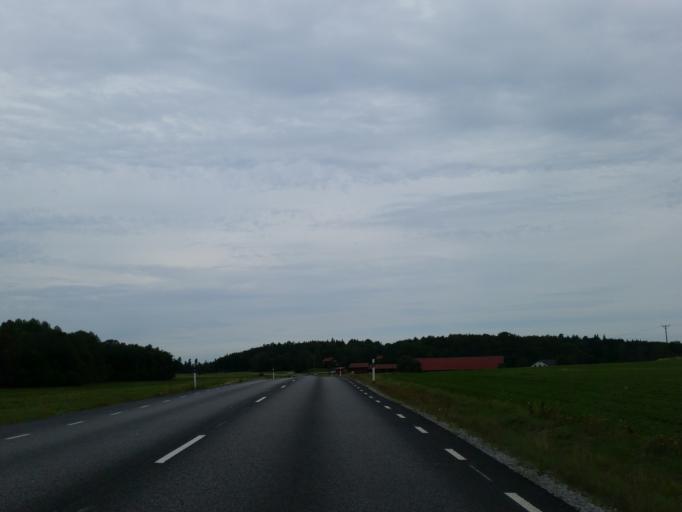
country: SE
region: Stockholm
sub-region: Salems Kommun
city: Ronninge
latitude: 59.2182
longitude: 17.7598
